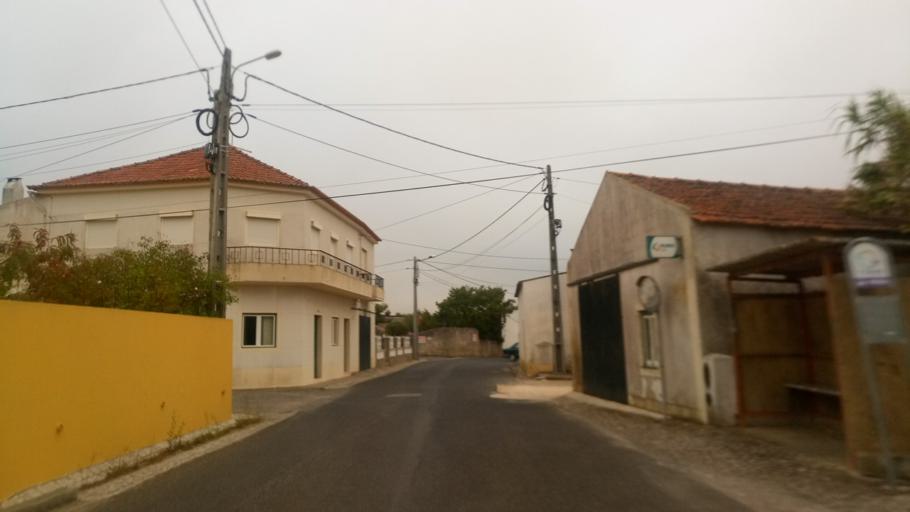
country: PT
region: Leiria
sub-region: Caldas da Rainha
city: Caldas da Rainha
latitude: 39.4519
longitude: -9.1784
